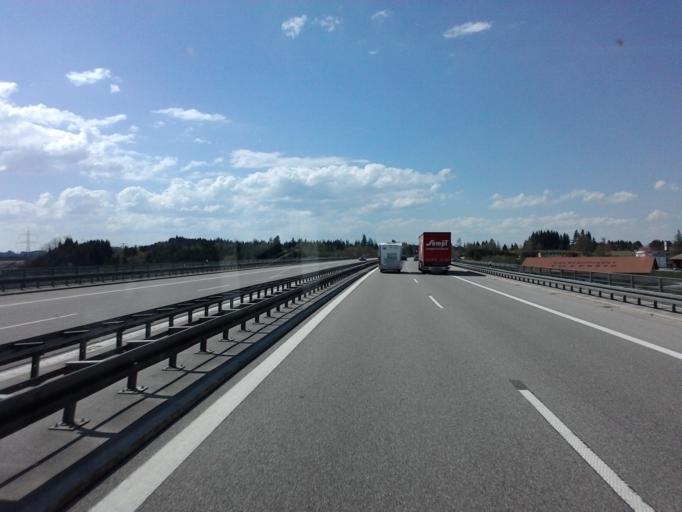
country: DE
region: Bavaria
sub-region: Swabia
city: Oy-Mittelberg
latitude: 47.6568
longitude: 10.4296
